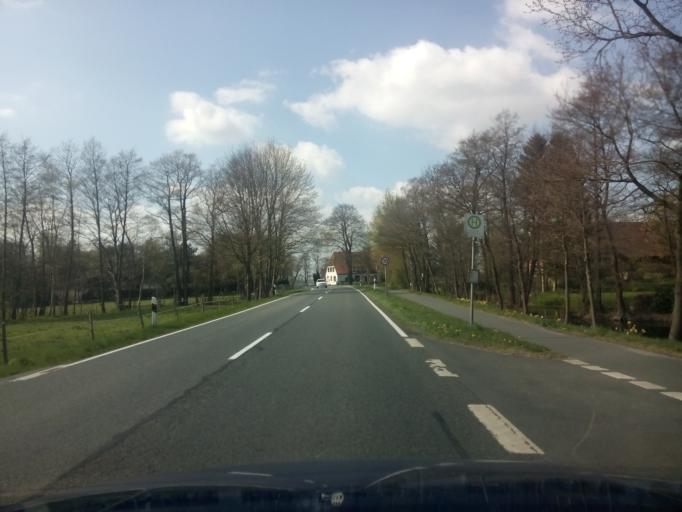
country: DE
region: Lower Saxony
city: Osterholz-Scharmbeck
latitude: 53.1827
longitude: 8.8477
